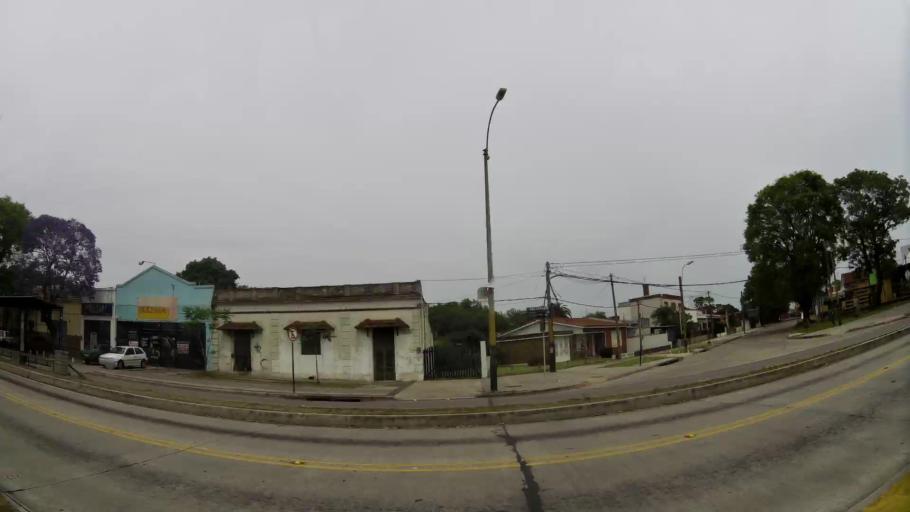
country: UY
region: Canelones
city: La Paz
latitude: -34.8012
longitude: -56.2243
